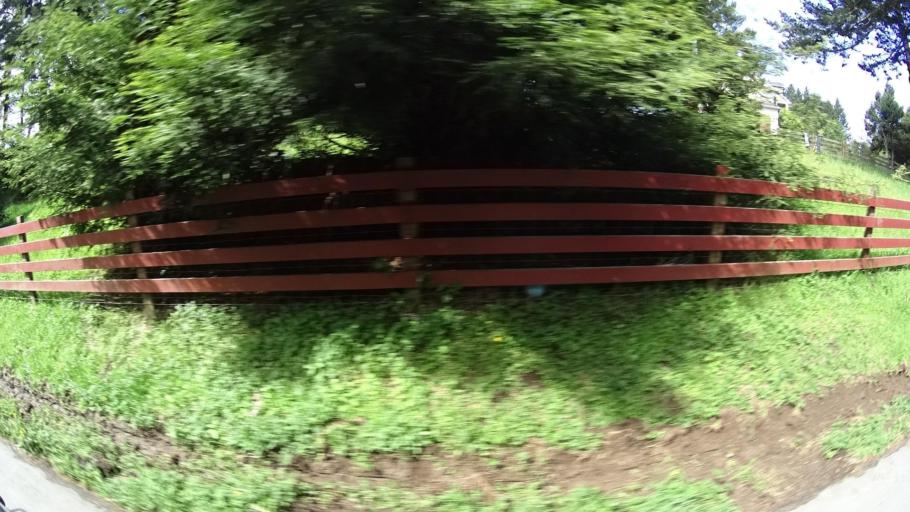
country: US
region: California
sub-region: Humboldt County
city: McKinleyville
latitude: 40.9228
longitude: -124.0800
